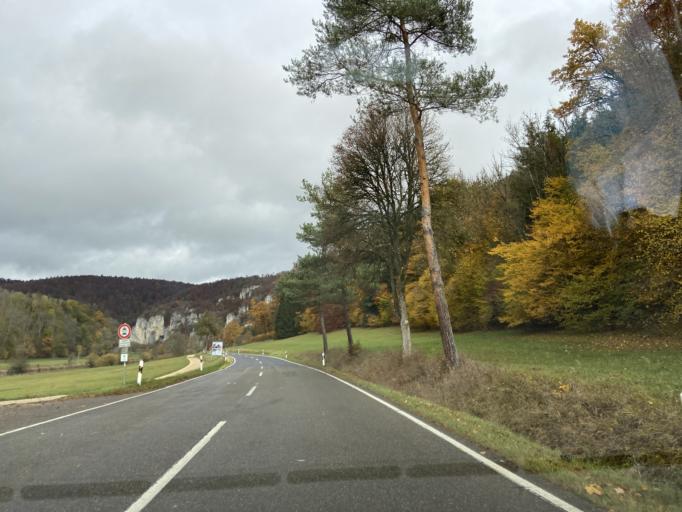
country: DE
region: Baden-Wuerttemberg
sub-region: Tuebingen Region
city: Stetten am Kalten Markt
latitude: 48.0836
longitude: 9.1066
